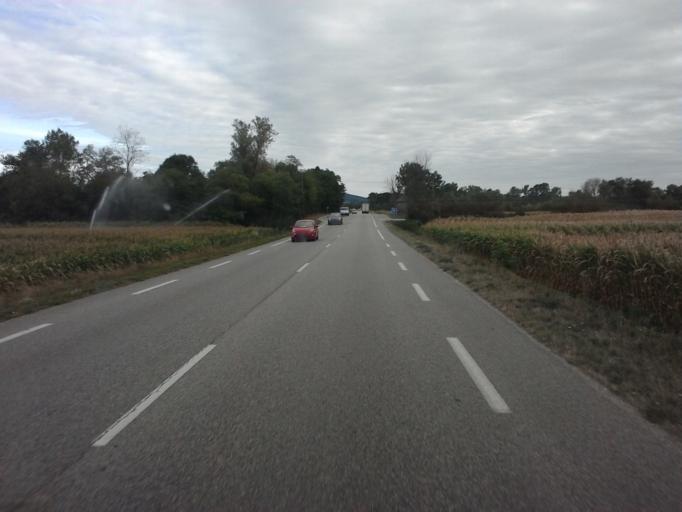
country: FR
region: Rhone-Alpes
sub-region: Departement de l'Ain
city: Ambronay
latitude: 46.0254
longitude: 5.3388
